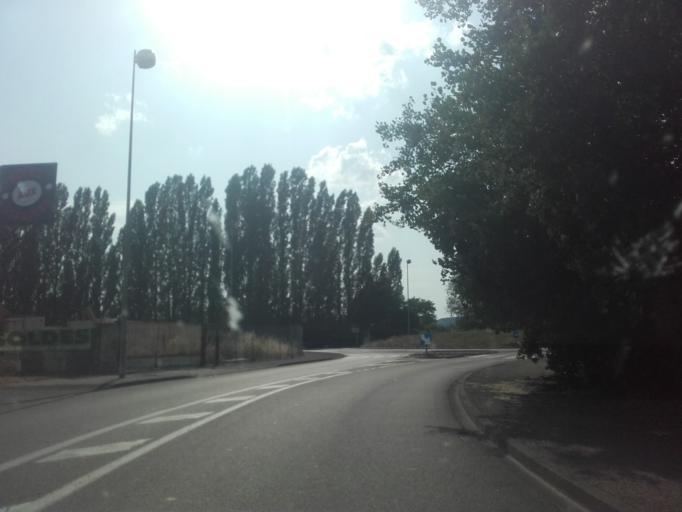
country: FR
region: Bourgogne
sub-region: Departement de la Cote-d'Or
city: Beaune
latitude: 47.0238
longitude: 4.8591
